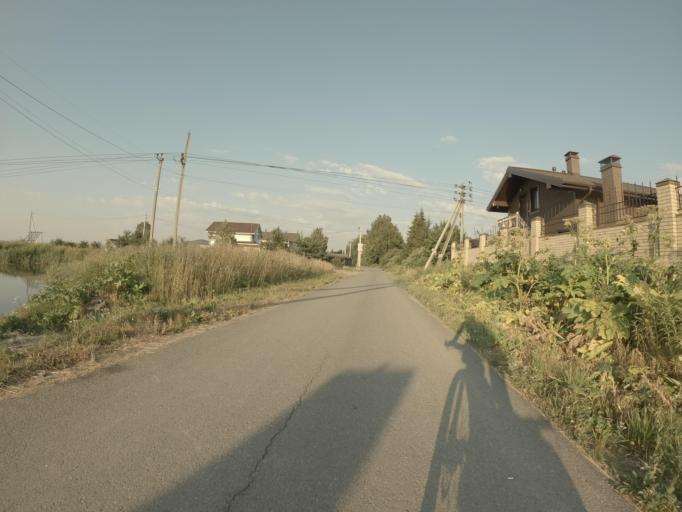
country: RU
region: Leningrad
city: Koltushi
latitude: 59.8890
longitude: 30.7063
